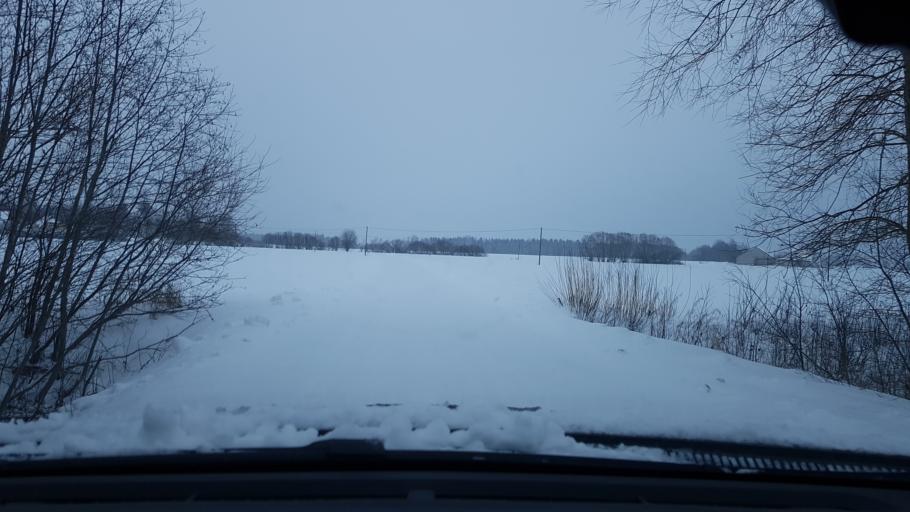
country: EE
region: Harju
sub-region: Anija vald
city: Kehra
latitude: 59.2483
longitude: 25.3533
